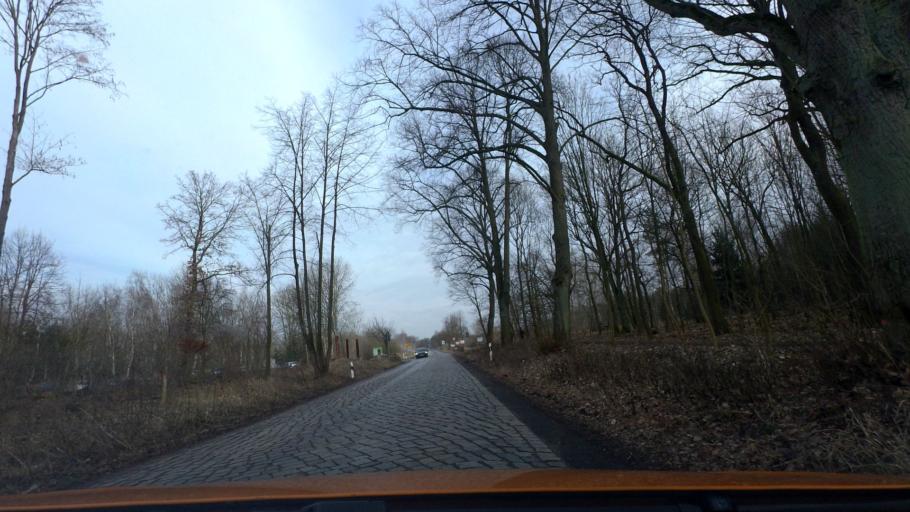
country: DE
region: Berlin
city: Buch
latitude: 52.6564
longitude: 13.4874
